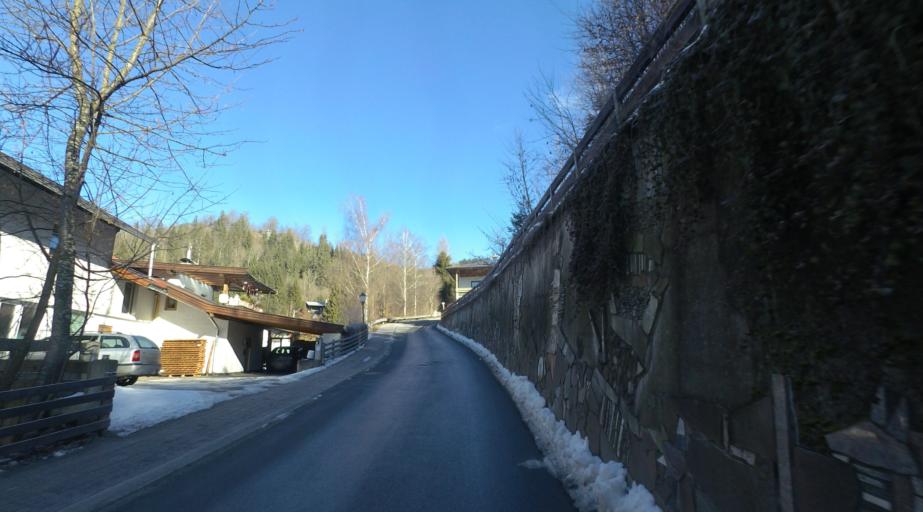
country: AT
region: Tyrol
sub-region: Politischer Bezirk Kitzbuhel
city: Kossen
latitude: 47.6701
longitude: 12.4069
